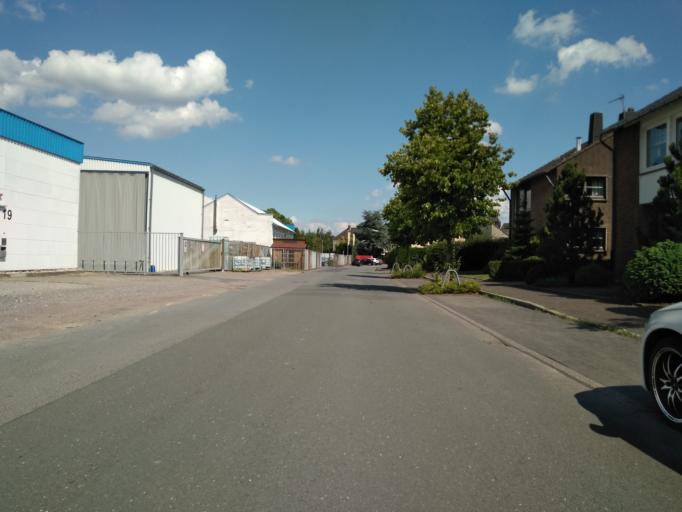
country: DE
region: North Rhine-Westphalia
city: Dorsten
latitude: 51.6714
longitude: 6.9662
